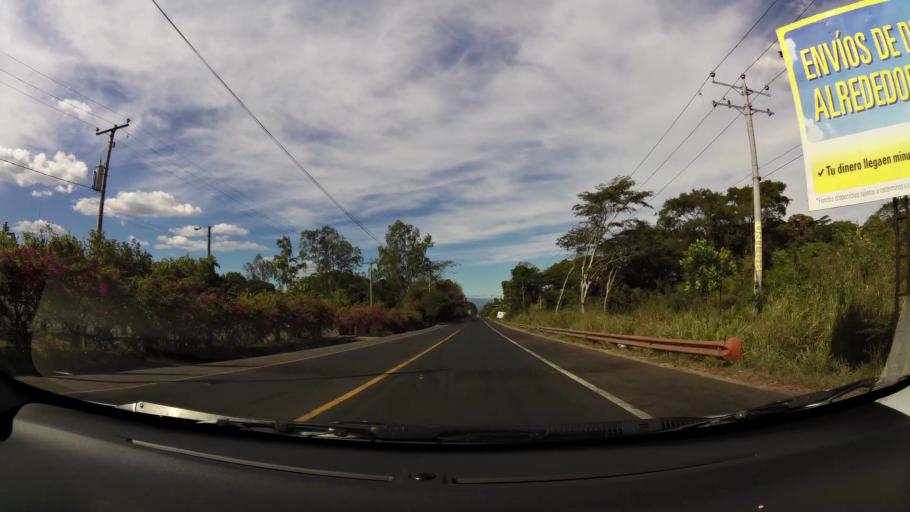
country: SV
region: San Salvador
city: Guazapa
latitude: 13.8956
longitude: -89.1780
